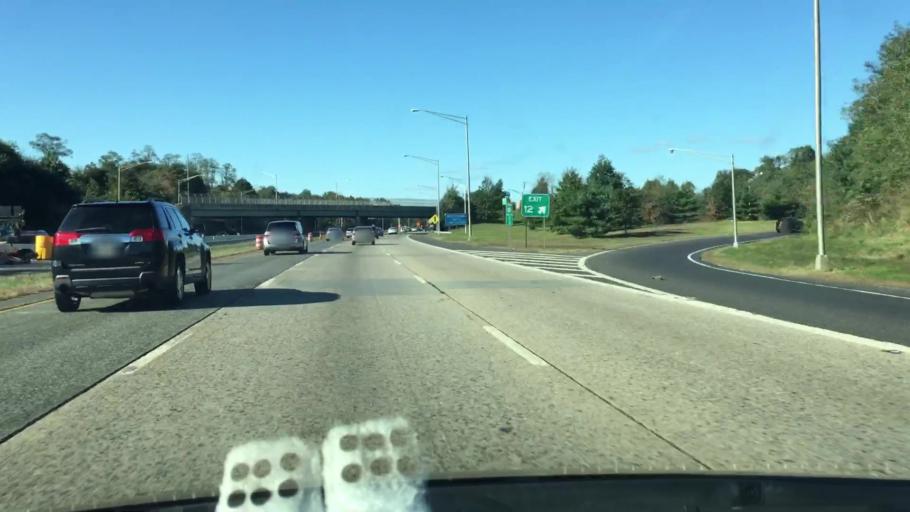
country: US
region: New Jersey
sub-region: Camden County
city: Glendora
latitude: 39.8295
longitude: -75.0874
